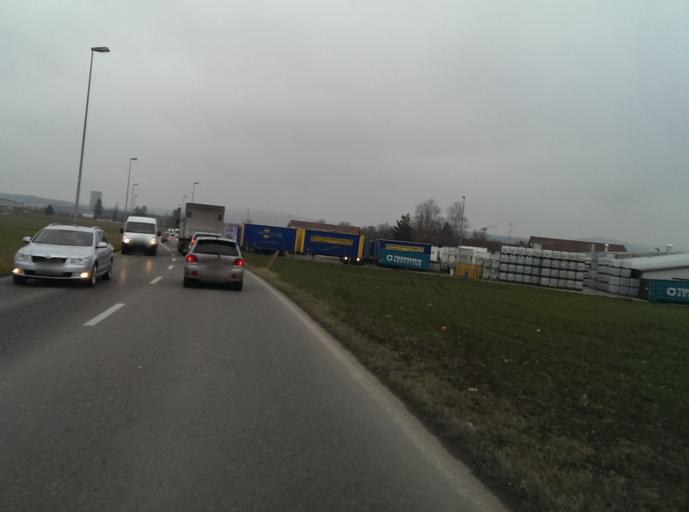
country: CH
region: Zurich
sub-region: Bezirk Dietikon
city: Dietikon / Almend
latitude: 47.4167
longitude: 8.3800
